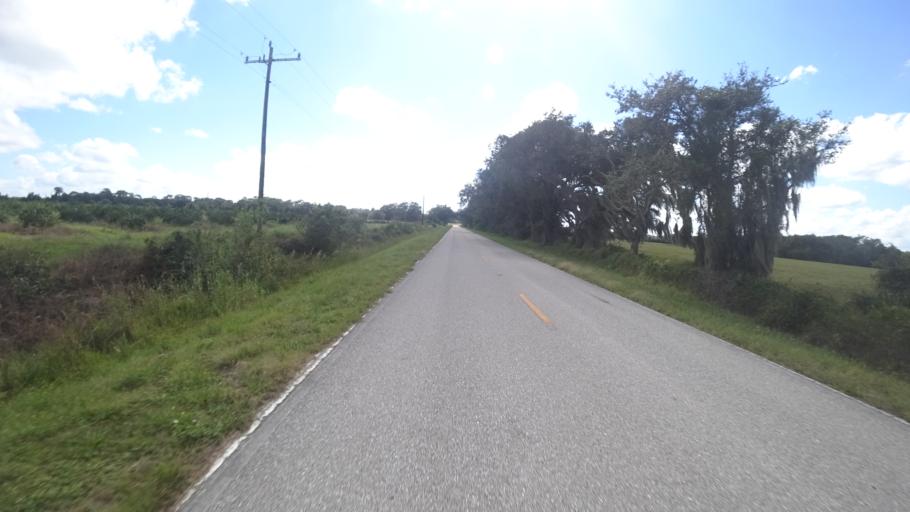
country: US
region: Florida
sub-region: Sarasota County
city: Lake Sarasota
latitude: 27.3285
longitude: -82.1667
